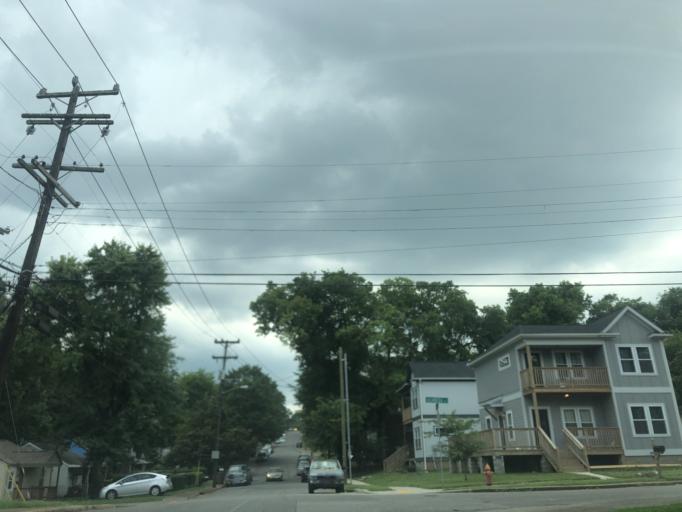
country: US
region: Tennessee
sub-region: Davidson County
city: Nashville
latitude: 36.1668
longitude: -86.8124
